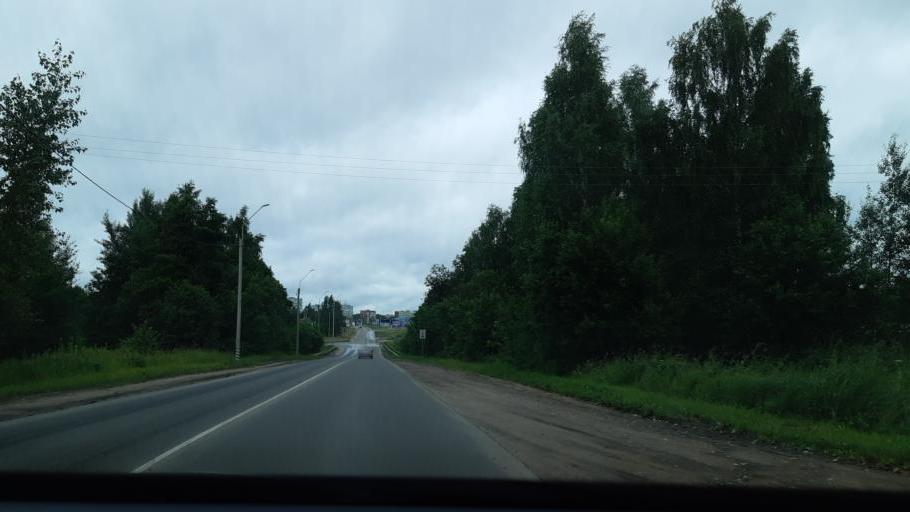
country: RU
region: Smolensk
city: Desnogorsk
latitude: 54.1377
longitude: 33.2779
